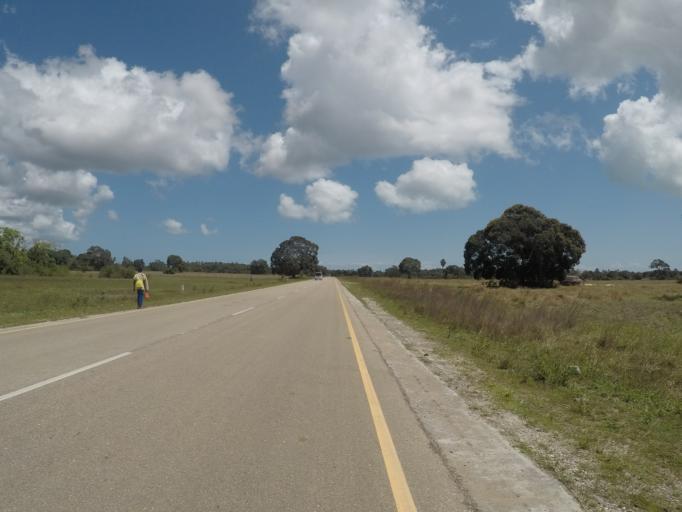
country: TZ
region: Zanzibar Central/South
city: Koani
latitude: -6.2224
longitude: 39.3622
